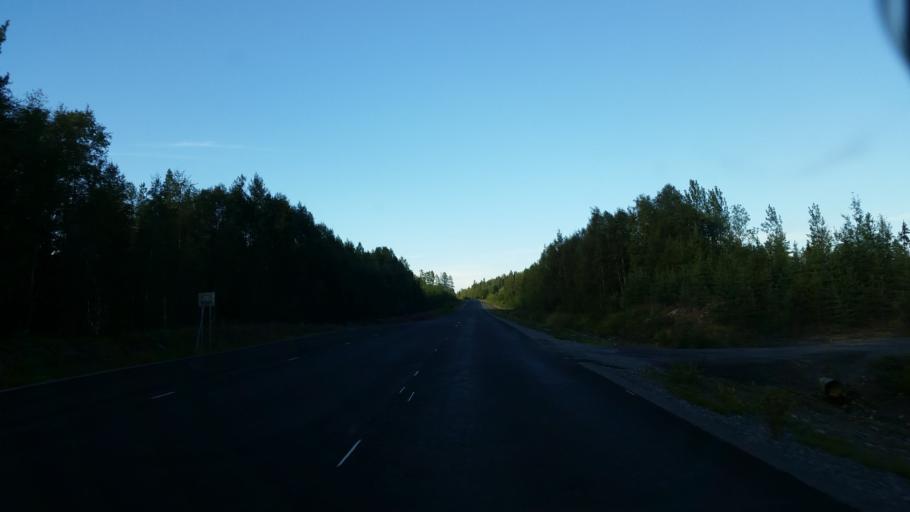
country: SE
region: Vaesterbotten
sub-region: Dorotea Kommun
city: Dorotea
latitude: 64.2996
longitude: 16.5610
